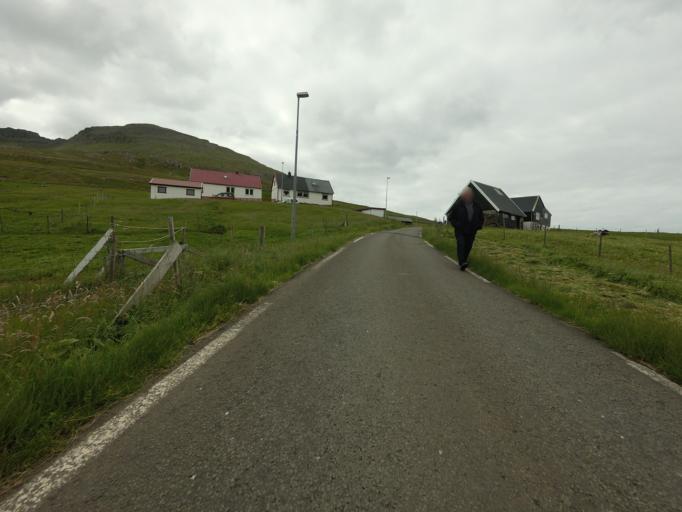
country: FO
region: Suduroy
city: Tvoroyri
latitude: 61.5214
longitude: -6.8808
